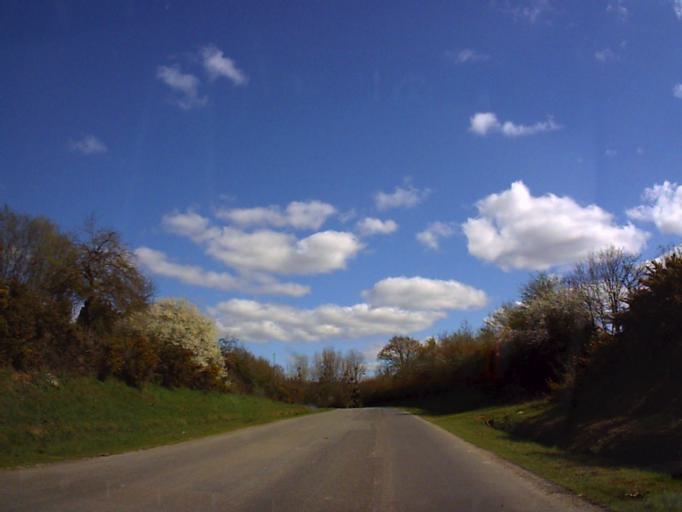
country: FR
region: Brittany
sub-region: Departement d'Ille-et-Vilaine
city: Gael
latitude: 48.1203
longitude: -2.1454
